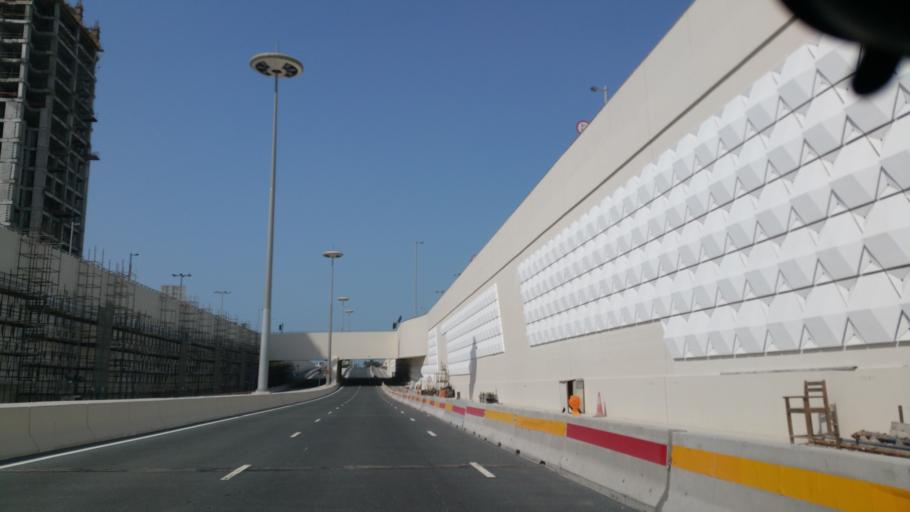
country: QA
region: Baladiyat Umm Salal
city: Umm Salal Muhammad
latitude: 25.4286
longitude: 51.5110
